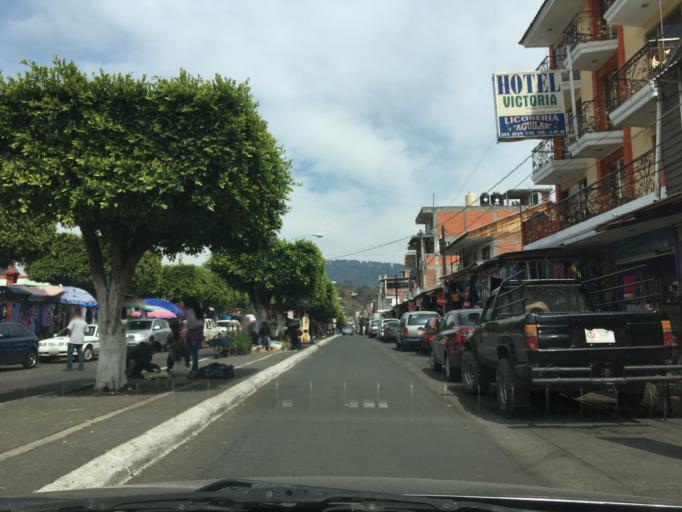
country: MX
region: Michoacan
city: Nuevo San Juan Parangaricutiro
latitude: 19.4161
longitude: -102.1287
